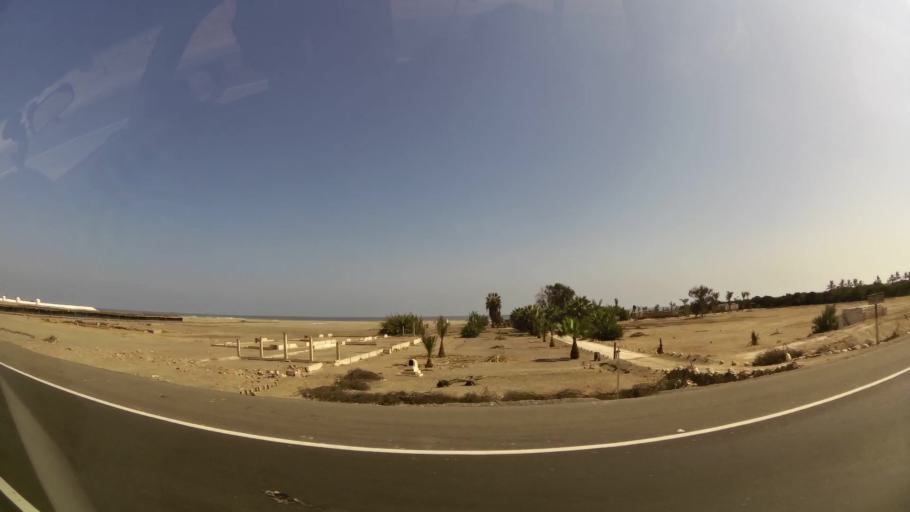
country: PE
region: Ica
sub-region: Provincia de Chincha
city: San Pedro
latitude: -13.3754
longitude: -76.2085
